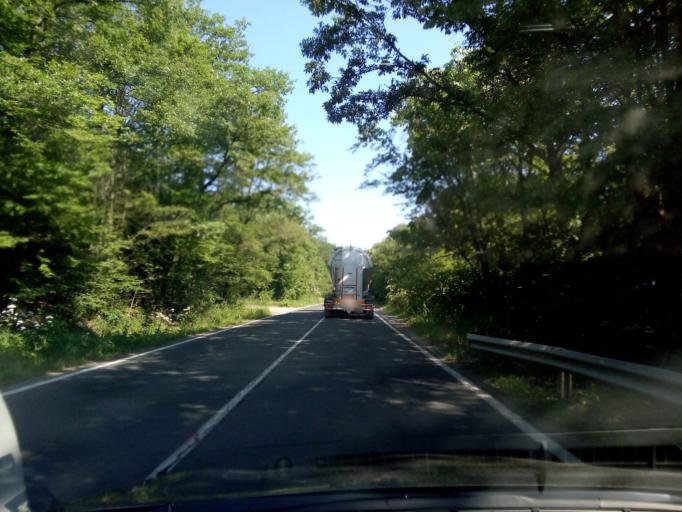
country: BG
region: Burgas
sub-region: Obshtina Nesebur
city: Sveti Vlas
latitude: 42.7721
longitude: 27.7682
